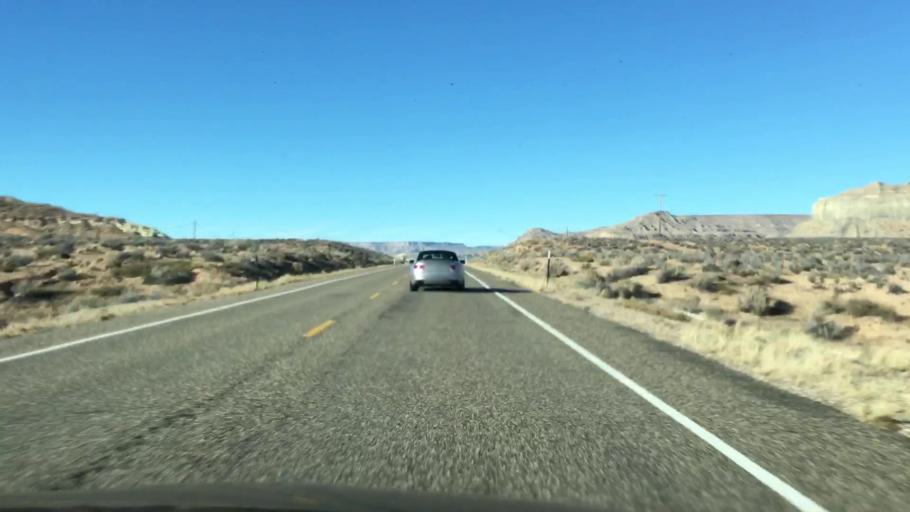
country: US
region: Arizona
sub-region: Coconino County
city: Page
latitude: 37.0422
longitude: -111.6199
